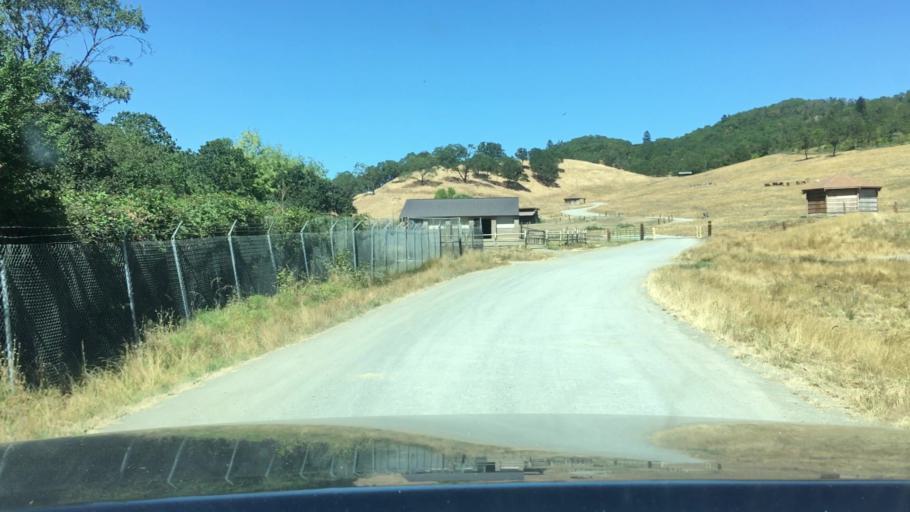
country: US
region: Oregon
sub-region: Douglas County
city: Winston
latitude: 43.1340
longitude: -123.4344
